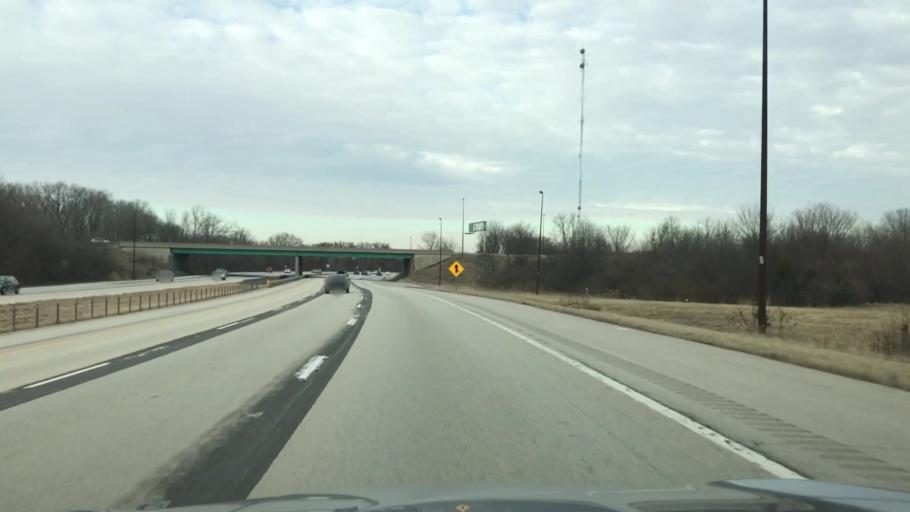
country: US
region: Illinois
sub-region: Sangamon County
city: Chatham
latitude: 39.6846
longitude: -89.6426
